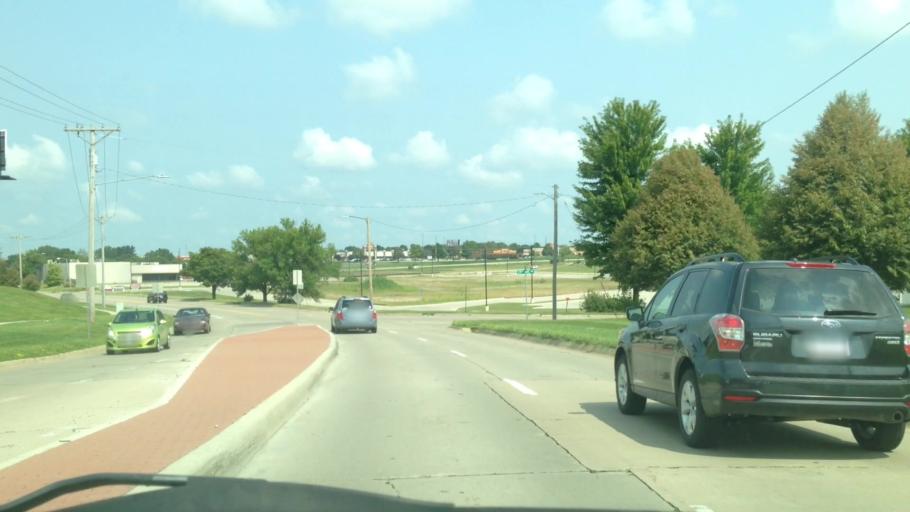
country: US
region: Iowa
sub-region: Linn County
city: Fairfax
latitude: 41.9485
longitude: -91.7211
